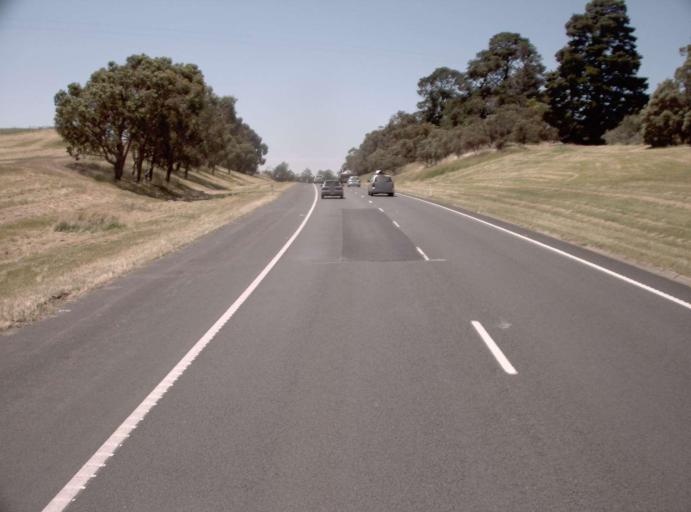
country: AU
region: Victoria
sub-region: Cardinia
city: Bunyip
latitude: -38.0772
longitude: 145.7365
